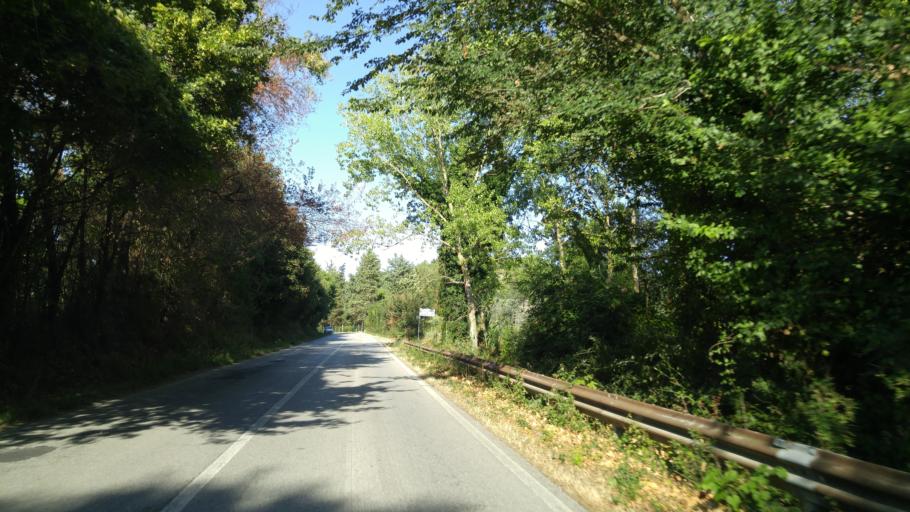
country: IT
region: The Marches
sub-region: Provincia di Pesaro e Urbino
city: Pesaro
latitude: 43.8728
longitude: 12.8894
